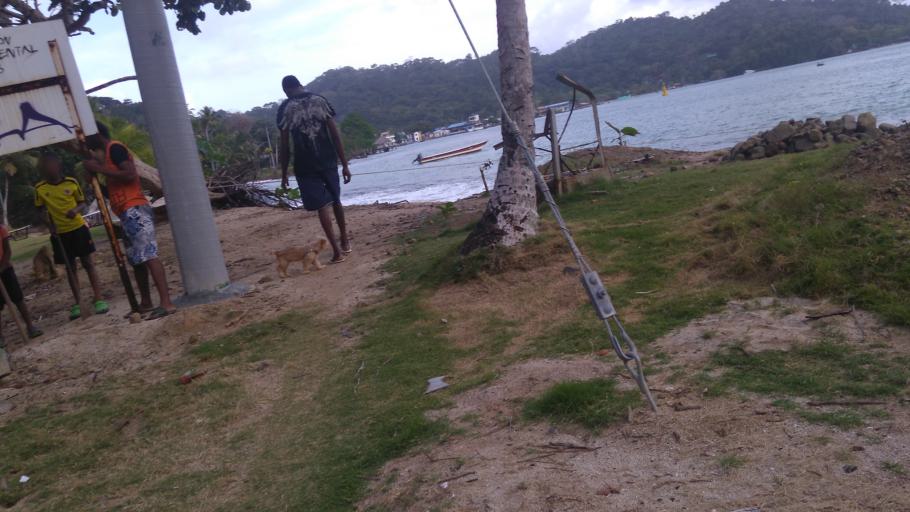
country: PA
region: Guna Yala
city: Puerto Obaldia
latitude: 8.6551
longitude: -77.3651
